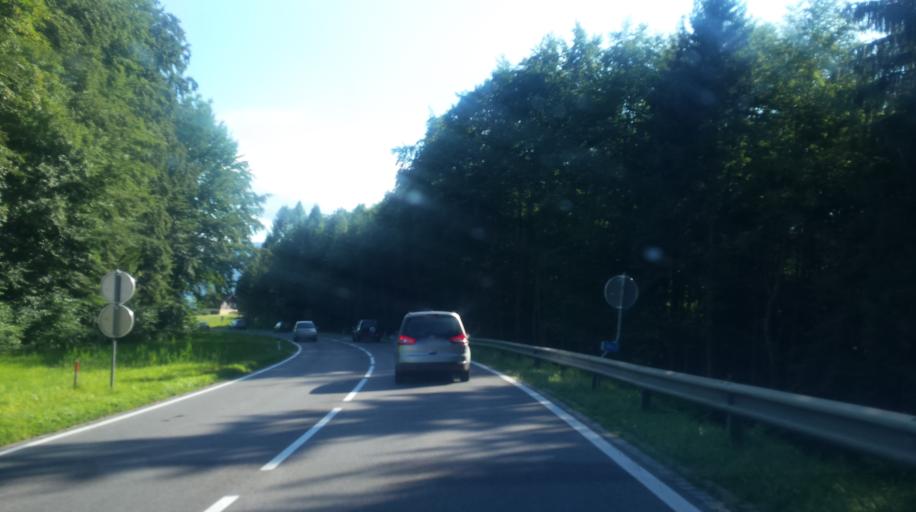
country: AT
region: Upper Austria
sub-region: Politischer Bezirk Gmunden
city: Gmunden
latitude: 47.9205
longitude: 13.7794
